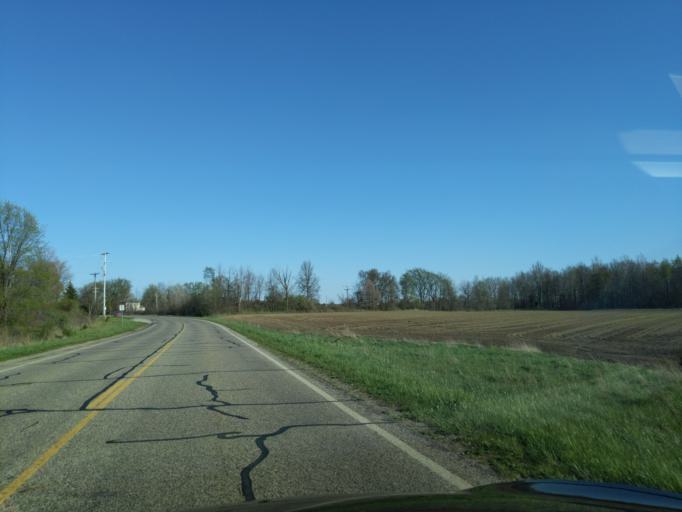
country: US
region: Michigan
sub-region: Ionia County
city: Portland
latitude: 42.8830
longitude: -84.9867
